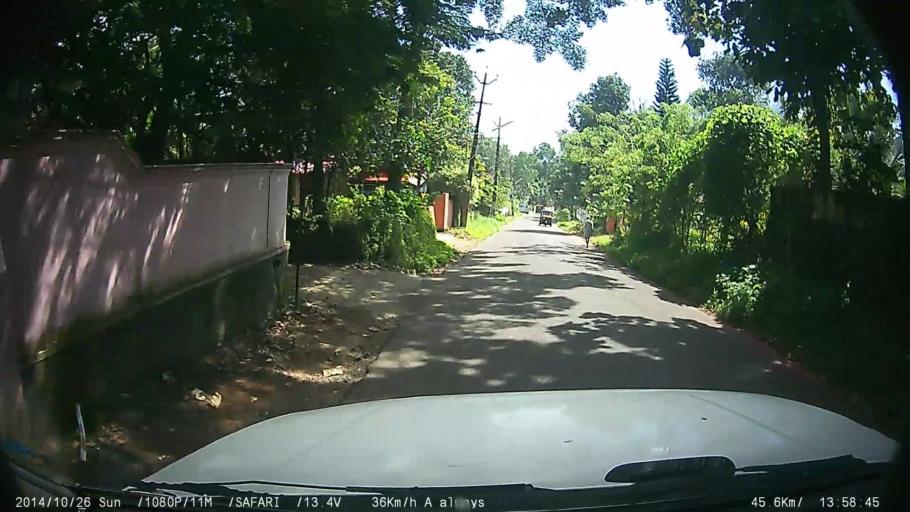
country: IN
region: Kerala
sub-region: Kottayam
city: Changanacheri
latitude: 9.4323
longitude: 76.5614
